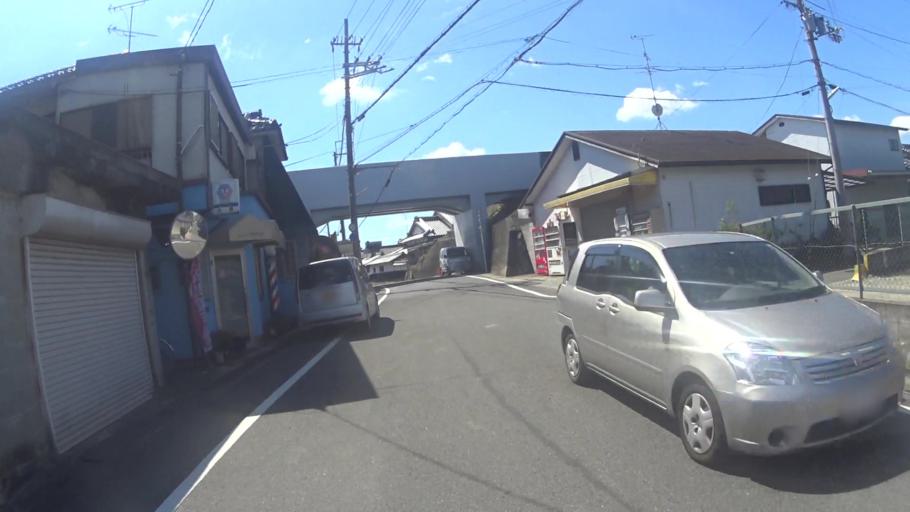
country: JP
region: Kyoto
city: Tanabe
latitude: 34.7918
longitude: 135.8103
